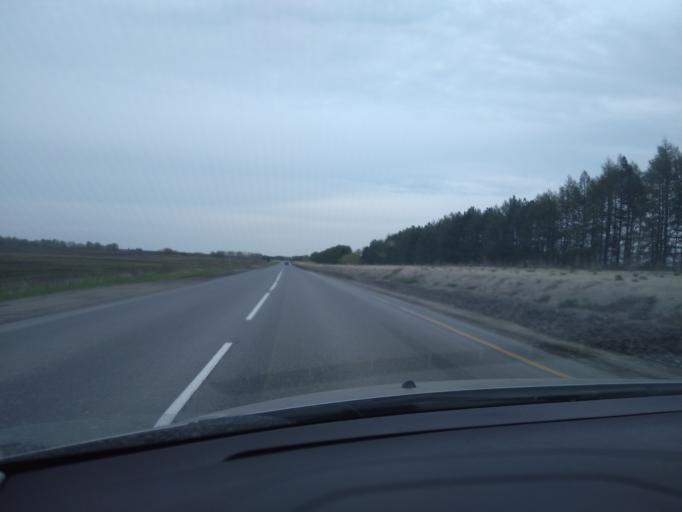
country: RU
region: Sverdlovsk
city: Kamyshlov
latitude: 56.8484
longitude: 62.8439
